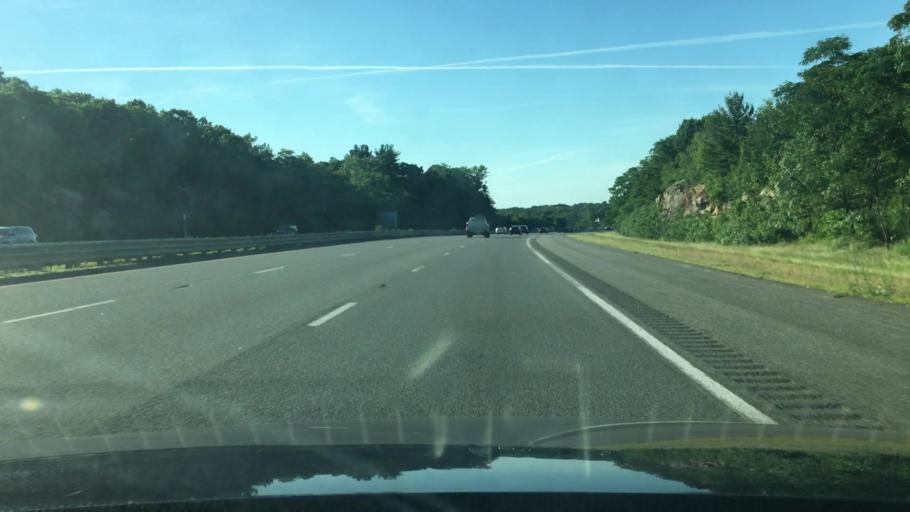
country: US
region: Massachusetts
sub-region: Essex County
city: South Peabody
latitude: 42.5362
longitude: -70.9837
